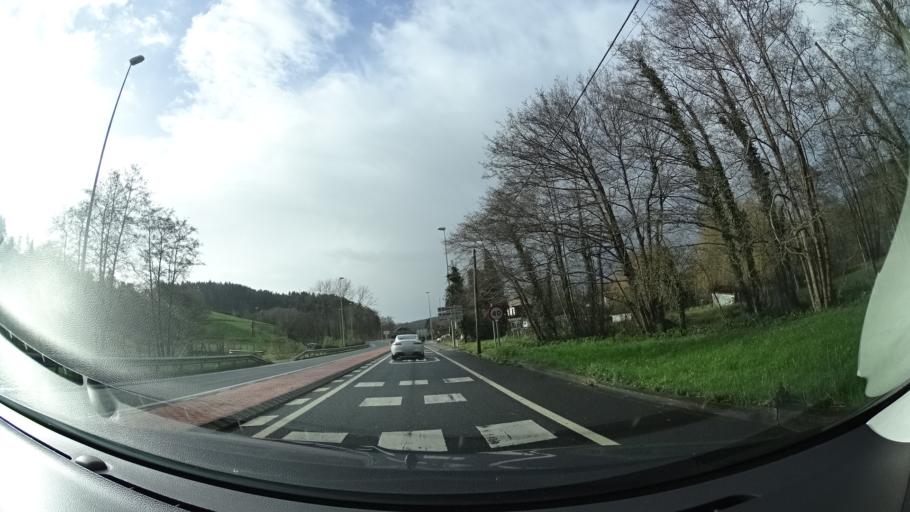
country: ES
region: Basque Country
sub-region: Bizkaia
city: Mungia
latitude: 43.3747
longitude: -2.8005
